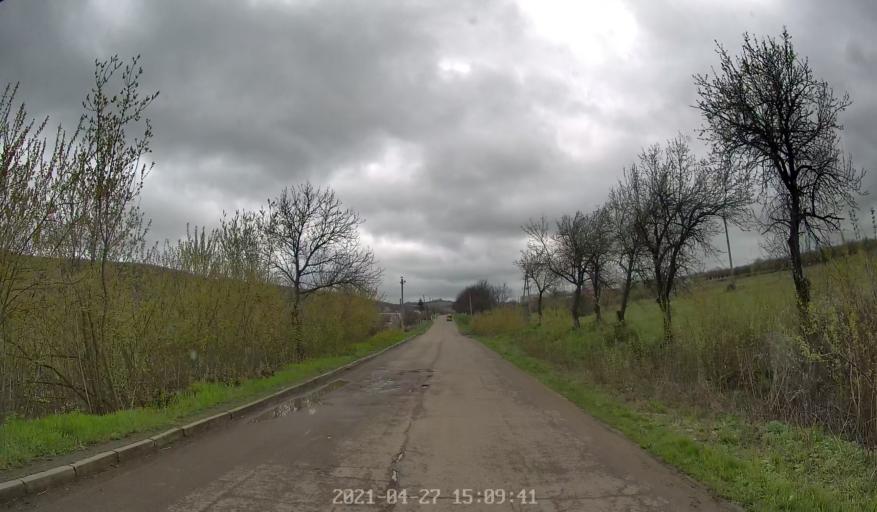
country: MD
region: Chisinau
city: Vadul lui Voda
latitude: 47.0475
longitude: 29.0337
